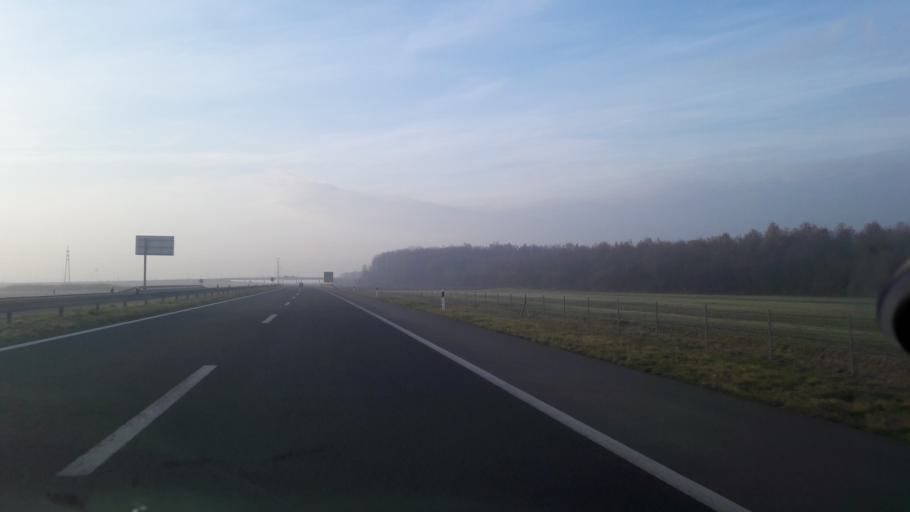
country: HR
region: Osjecko-Baranjska
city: Cepin
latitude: 45.5120
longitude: 18.5069
